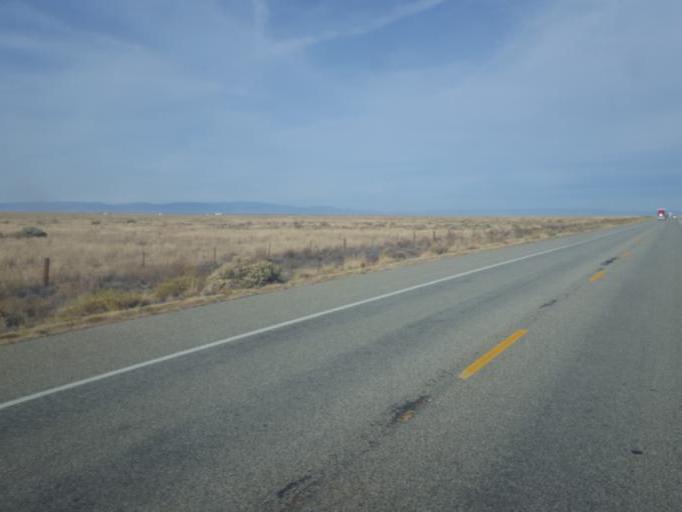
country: US
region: Colorado
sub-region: Alamosa County
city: Alamosa East
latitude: 37.4585
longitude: -105.5564
